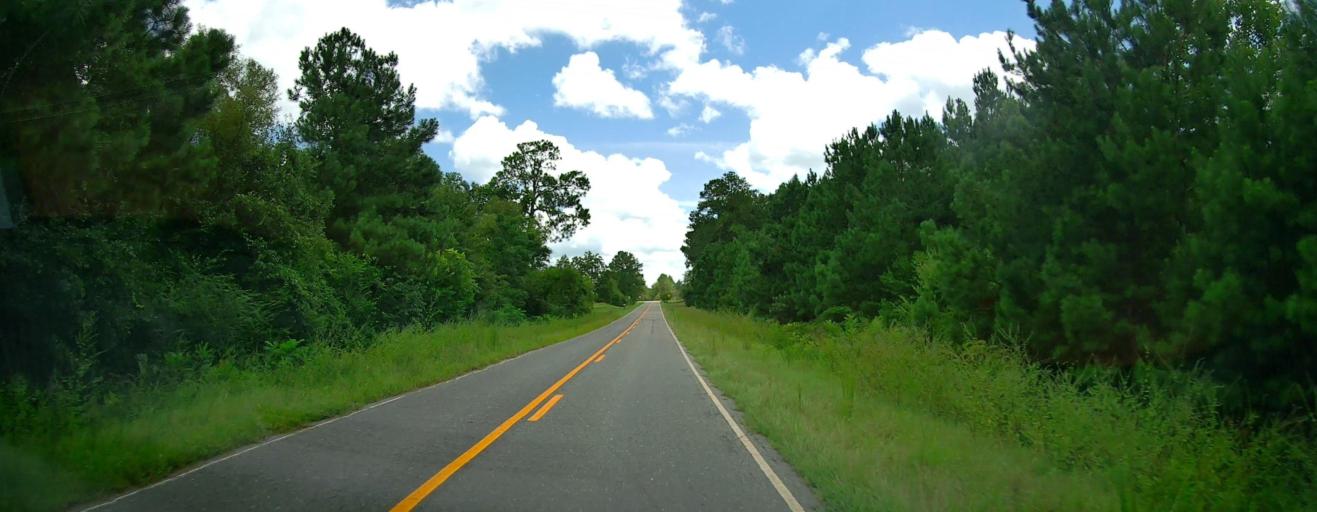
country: US
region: Georgia
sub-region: Irwin County
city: Ocilla
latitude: 31.6470
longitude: -83.3972
